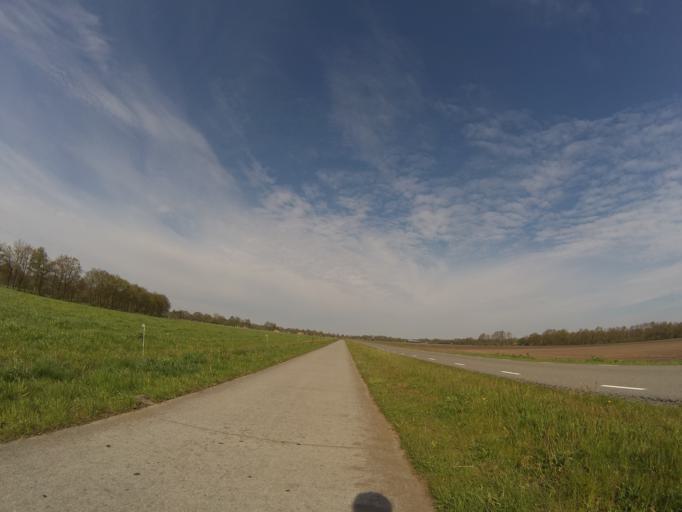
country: NL
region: Drenthe
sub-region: Gemeente Coevorden
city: Sleen
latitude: 52.7942
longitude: 6.7490
